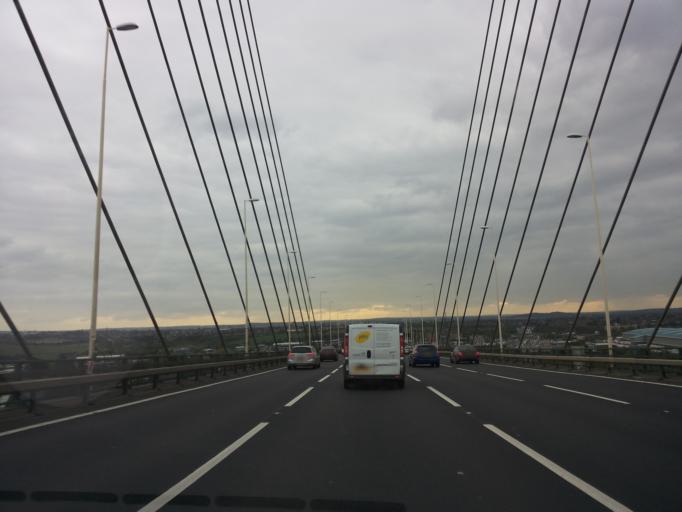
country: GB
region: England
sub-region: Kent
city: Stone
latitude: 51.4627
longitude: 0.2570
